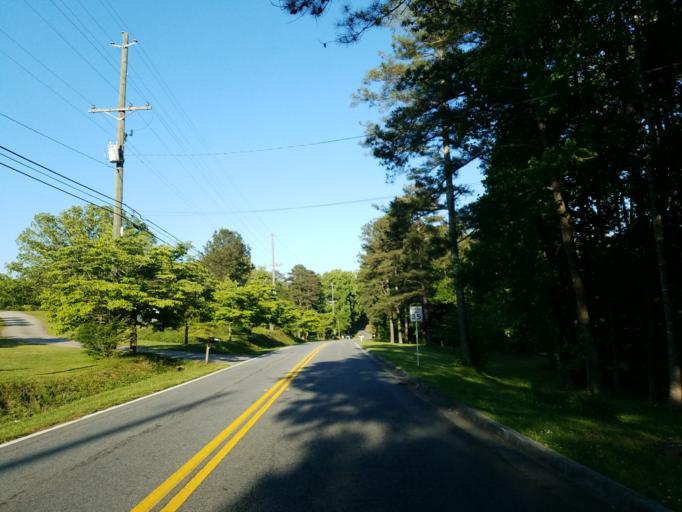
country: US
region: Georgia
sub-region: Cobb County
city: Mableton
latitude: 33.8319
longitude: -84.5433
